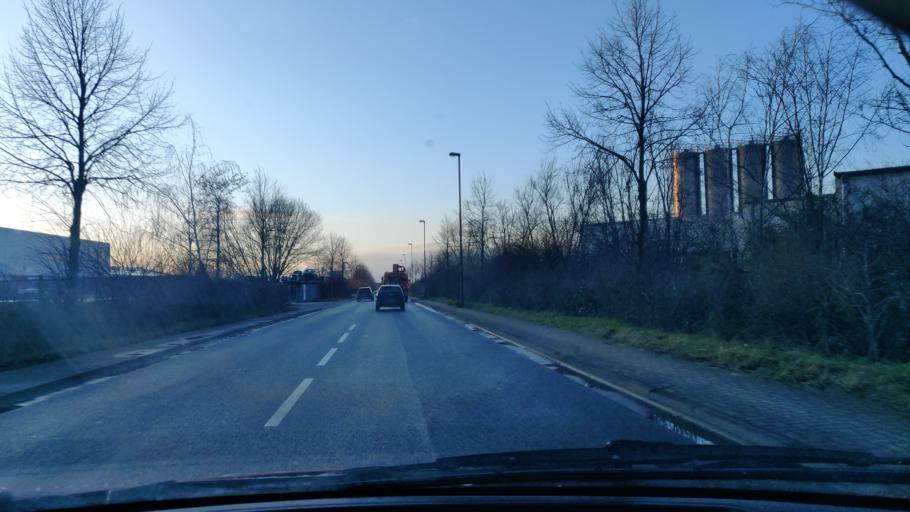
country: DE
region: North Rhine-Westphalia
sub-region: Regierungsbezirk Koln
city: Kerpen
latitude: 50.8964
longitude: 6.6537
